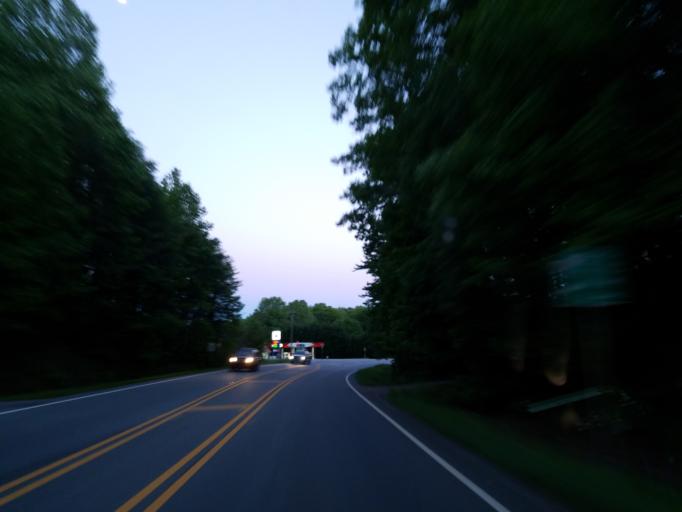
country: US
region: Georgia
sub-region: Lumpkin County
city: Dahlonega
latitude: 34.5663
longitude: -83.9668
